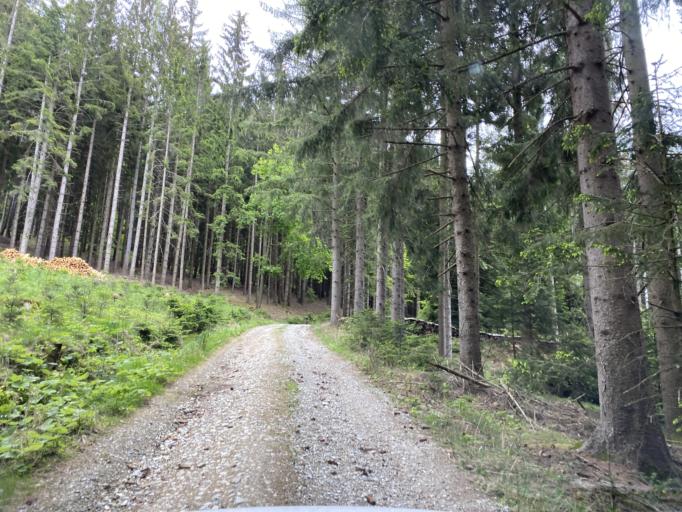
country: AT
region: Styria
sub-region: Politischer Bezirk Weiz
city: Baierdorf-Umgebung
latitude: 47.3073
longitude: 15.7050
